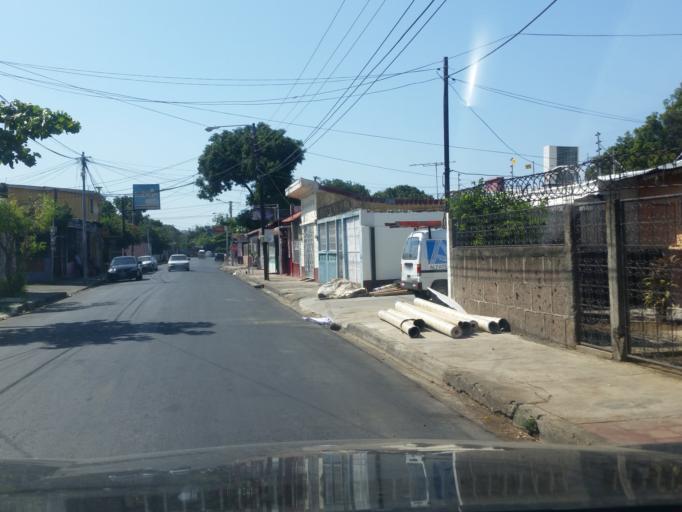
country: NI
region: Managua
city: Managua
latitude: 12.1480
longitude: -86.2916
